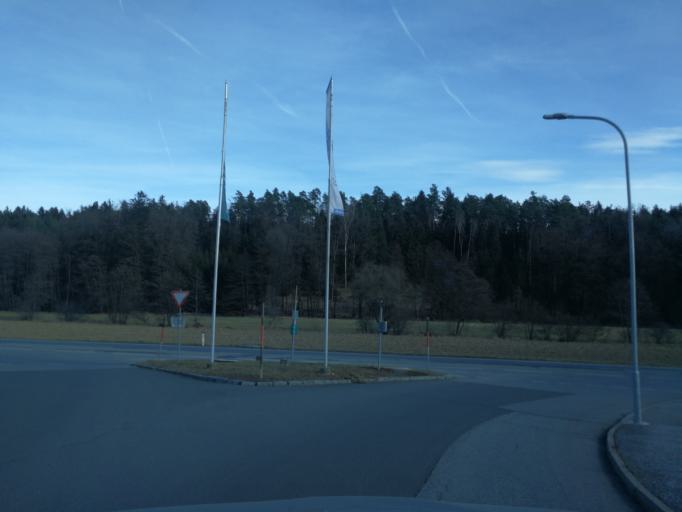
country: AT
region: Styria
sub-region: Politischer Bezirk Graz-Umgebung
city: Unterpremstatten
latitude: 46.9477
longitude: 15.3824
